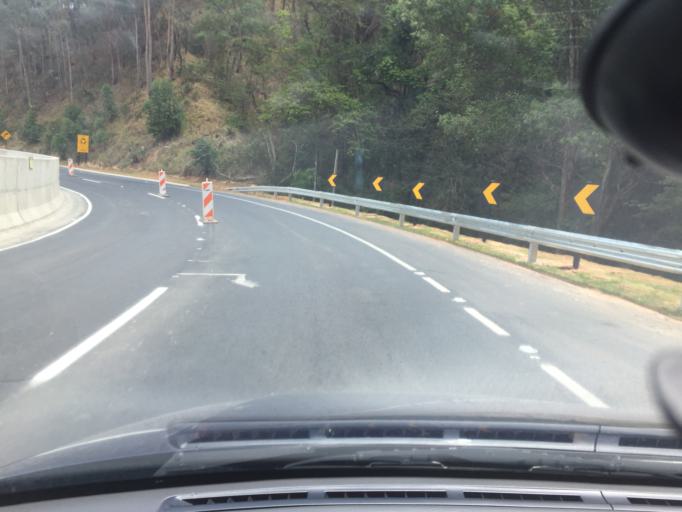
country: BR
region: Sao Paulo
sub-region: Jundiai
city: Jundiai
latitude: -23.1696
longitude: -46.8820
